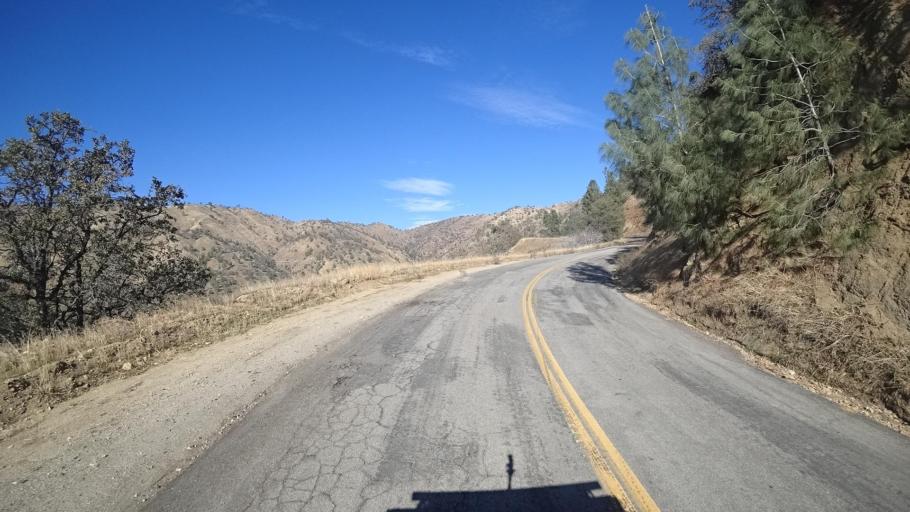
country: US
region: California
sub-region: Kern County
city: Bear Valley Springs
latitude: 35.3353
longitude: -118.5836
